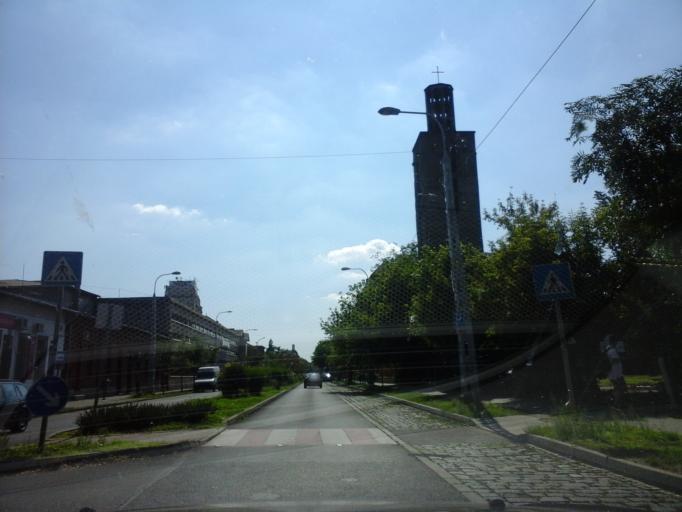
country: HU
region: Budapest
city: Budapest VIII. keruelet
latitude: 47.4836
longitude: 19.0993
